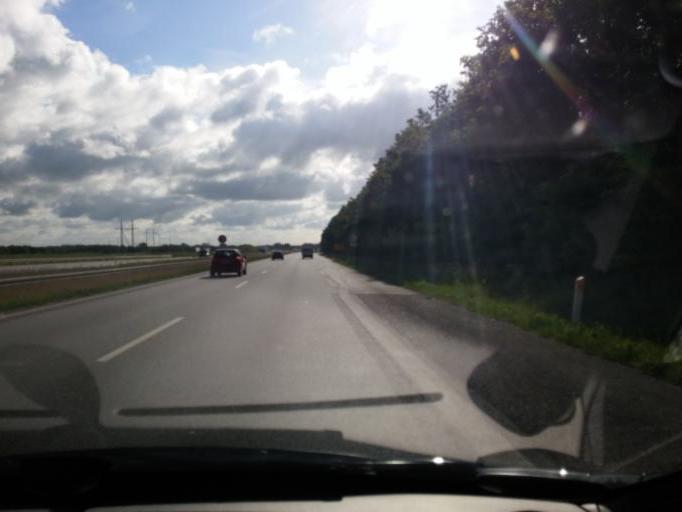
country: DK
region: Zealand
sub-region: Koge Kommune
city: Borup
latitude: 55.4565
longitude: 11.9253
